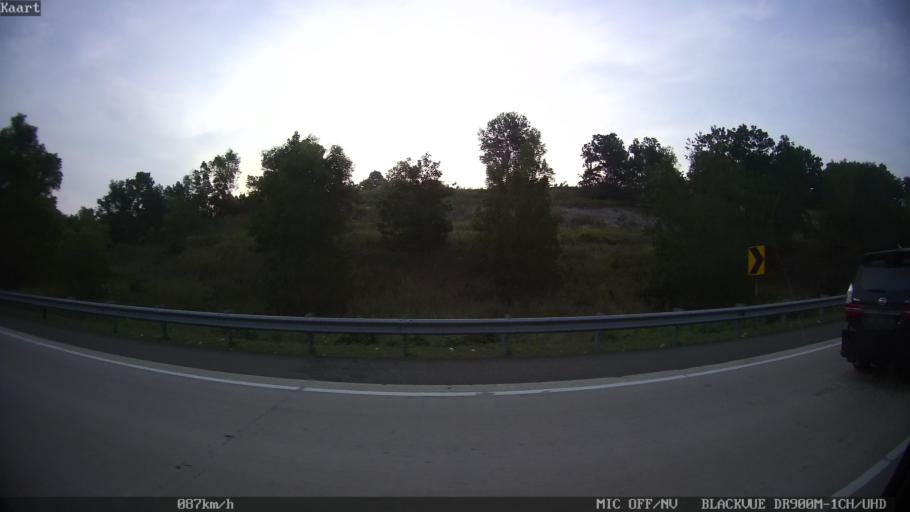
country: ID
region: Lampung
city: Penengahan
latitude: -5.8446
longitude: 105.7271
